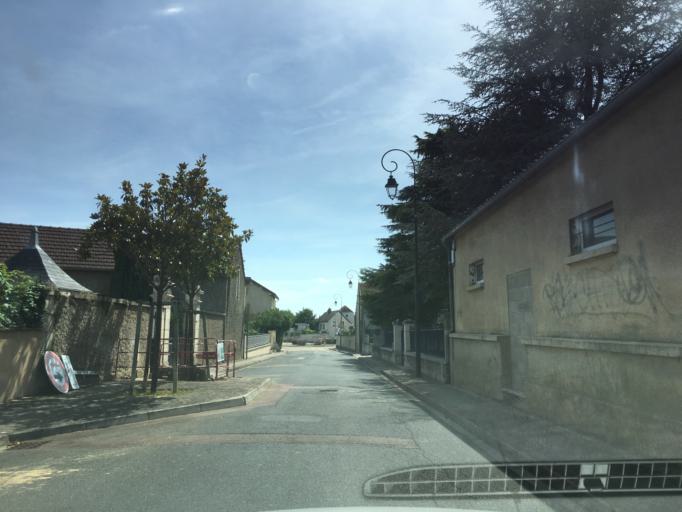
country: FR
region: Bourgogne
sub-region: Departement de l'Yonne
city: Saint-Georges-sur-Baulche
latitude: 47.8015
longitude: 3.5313
